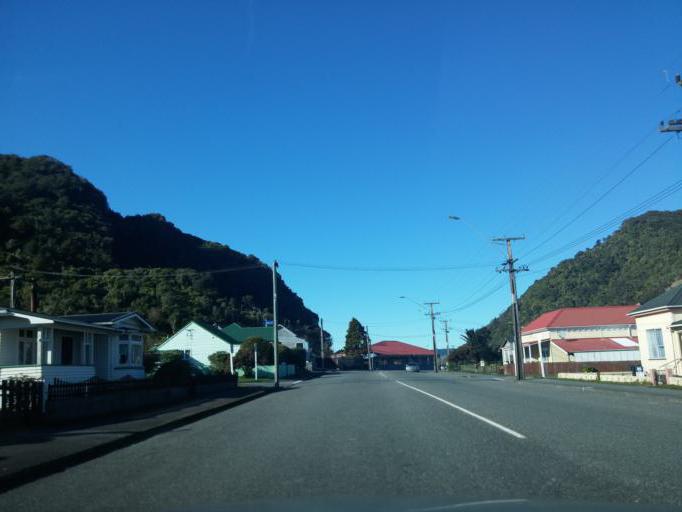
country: NZ
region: West Coast
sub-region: Grey District
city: Greymouth
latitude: -42.4441
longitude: 171.2142
